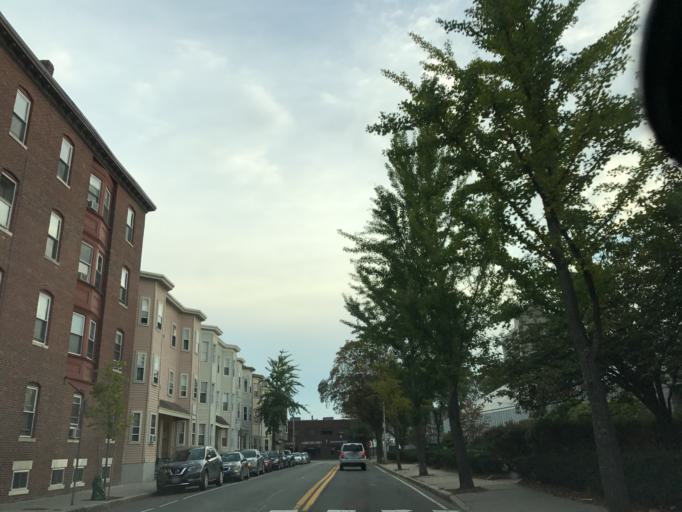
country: US
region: Massachusetts
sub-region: Middlesex County
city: Cambridge
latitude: 42.3710
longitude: -71.0890
